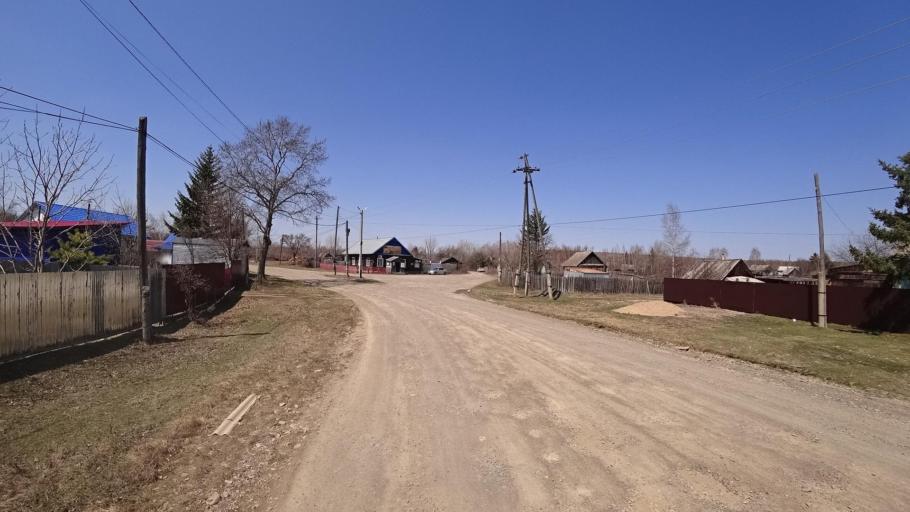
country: RU
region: Khabarovsk Krai
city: Khurba
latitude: 50.4092
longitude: 136.8659
